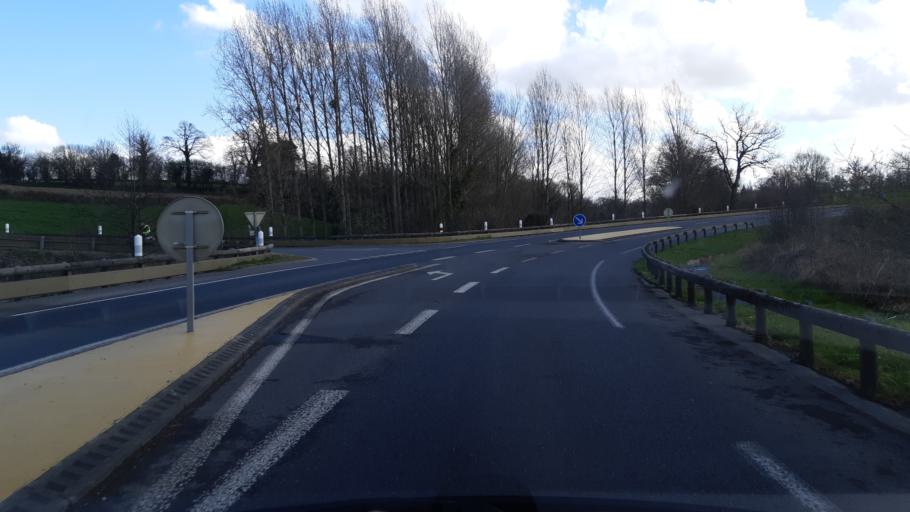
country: FR
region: Lower Normandy
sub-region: Departement de la Manche
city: Agneaux
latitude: 49.0700
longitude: -1.1300
